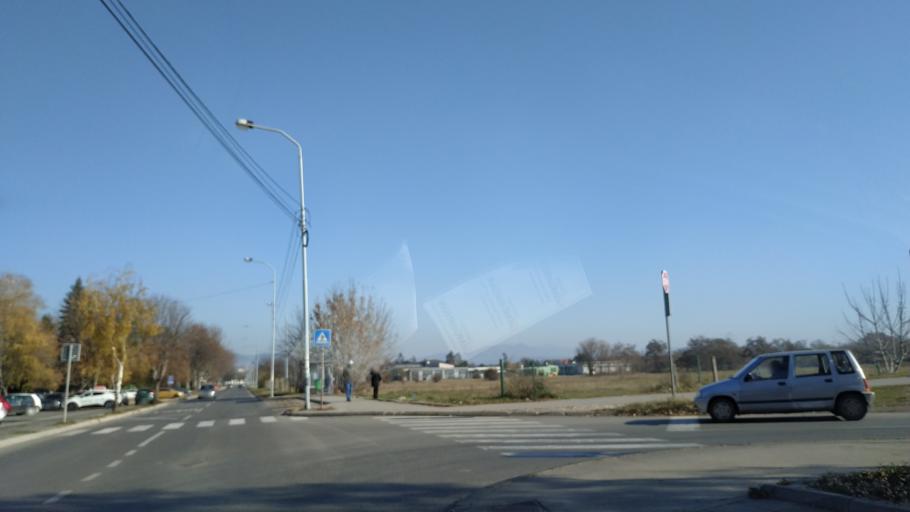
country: RS
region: Central Serbia
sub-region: Nisavski Okrug
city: Nis
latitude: 43.3297
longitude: 21.8913
